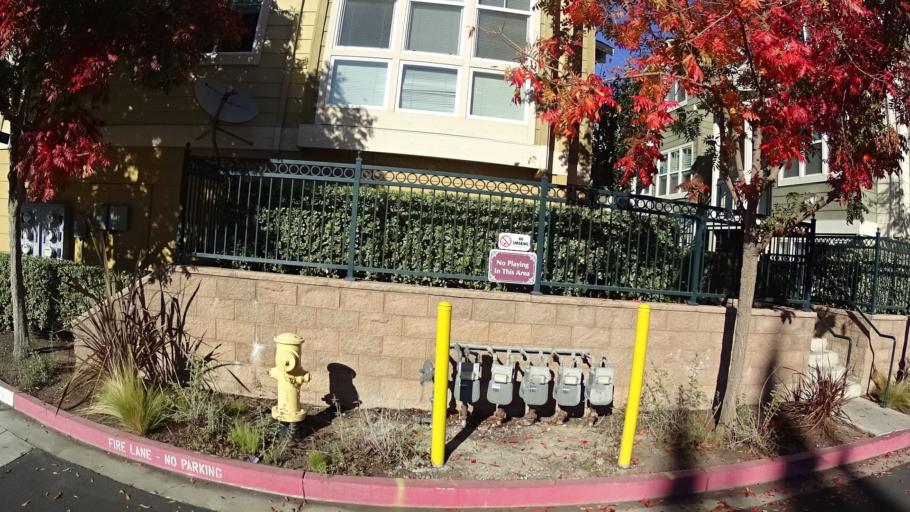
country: US
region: California
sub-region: Santa Clara County
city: Sunnyvale
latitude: 37.3688
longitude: -122.0002
